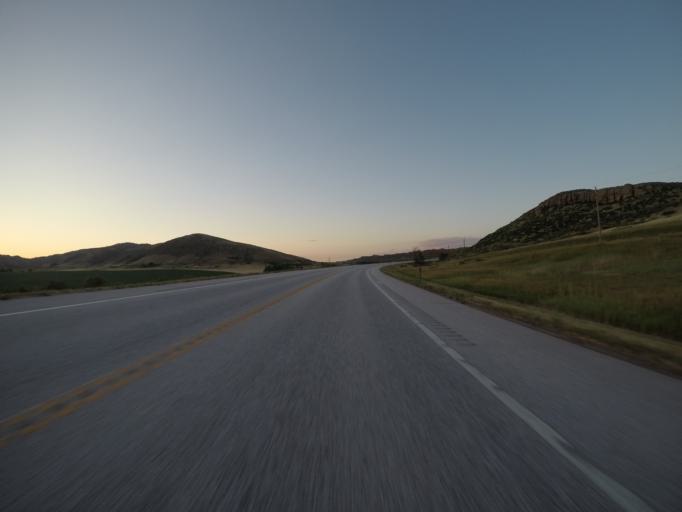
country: US
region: Colorado
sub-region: Larimer County
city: Laporte
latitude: 40.6705
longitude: -105.1909
